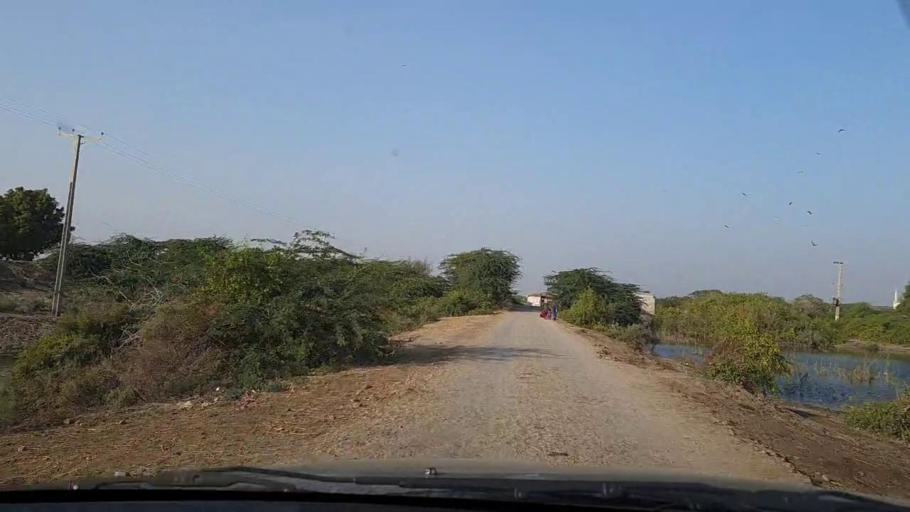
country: PK
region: Sindh
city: Chuhar Jamali
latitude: 24.2982
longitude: 67.7552
